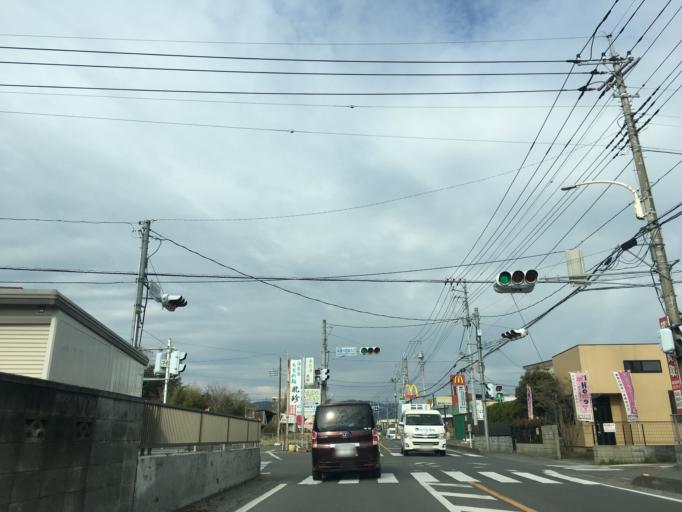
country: JP
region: Saitama
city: Hanno
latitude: 35.8981
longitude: 139.3517
